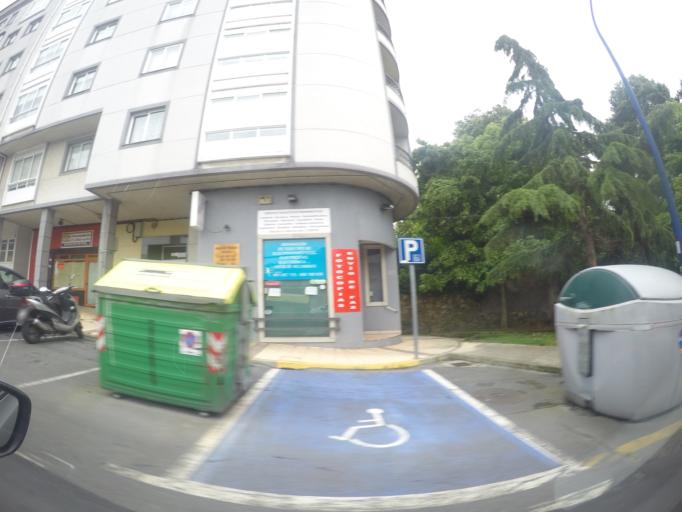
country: ES
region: Galicia
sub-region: Provincia da Coruna
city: Culleredo
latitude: 43.3100
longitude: -8.3827
